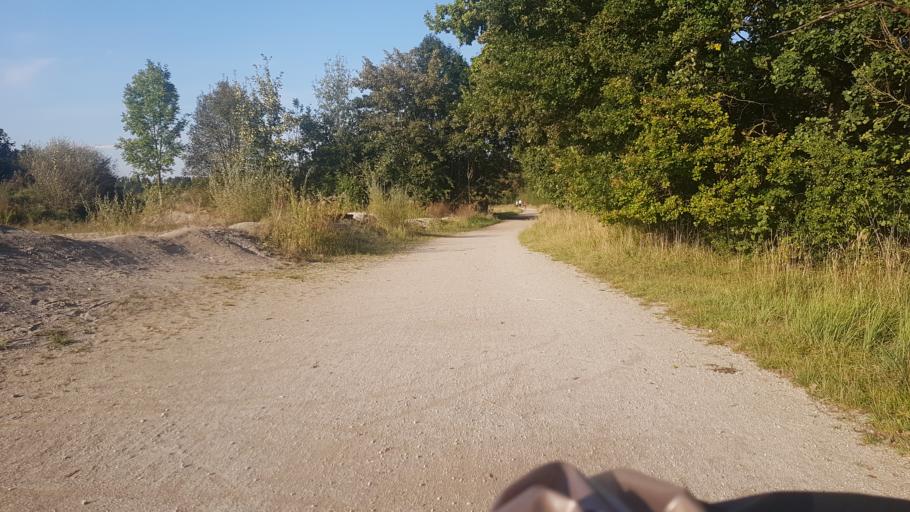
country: DE
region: Bavaria
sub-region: Upper Bavaria
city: Neubiberg
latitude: 48.0950
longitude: 11.6643
